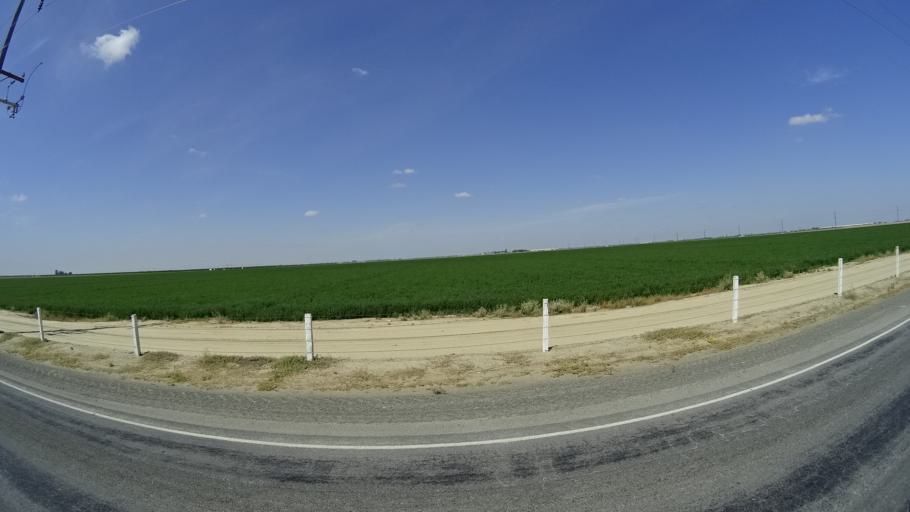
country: US
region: California
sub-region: Tulare County
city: Goshen
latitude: 36.2943
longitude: -119.4921
